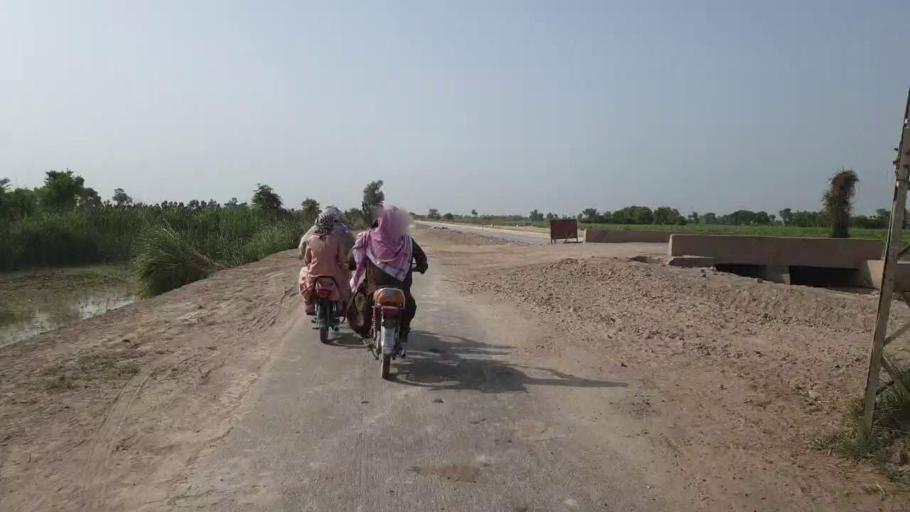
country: PK
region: Sindh
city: Daur
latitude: 26.3363
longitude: 68.1638
